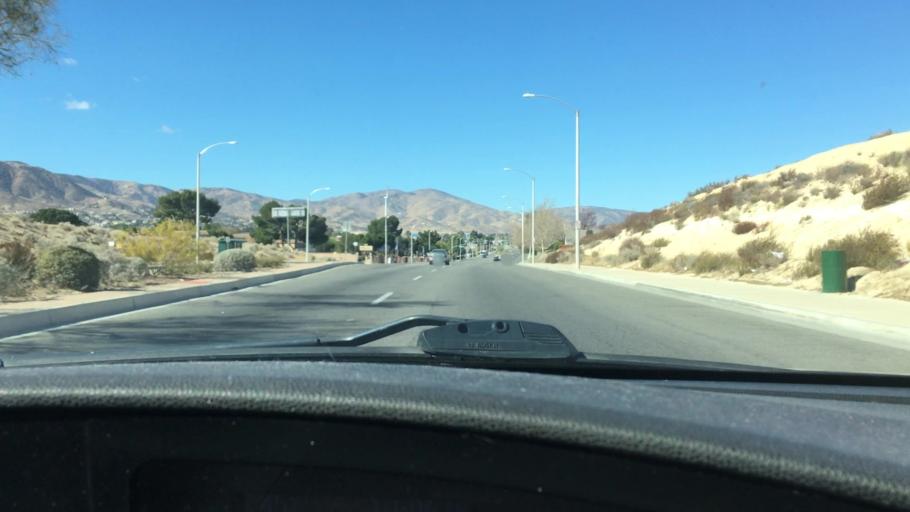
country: US
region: California
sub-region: Los Angeles County
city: Palmdale
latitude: 34.5582
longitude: -118.1014
